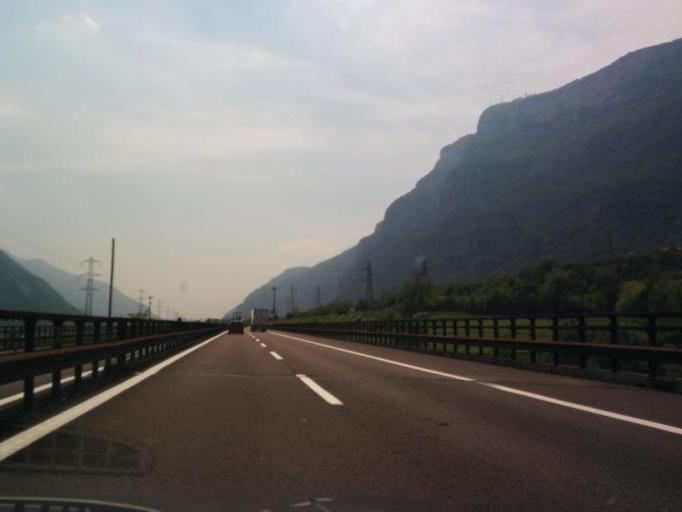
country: IT
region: Veneto
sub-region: Provincia di Verona
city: Rivalta
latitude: 45.6439
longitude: 10.8815
